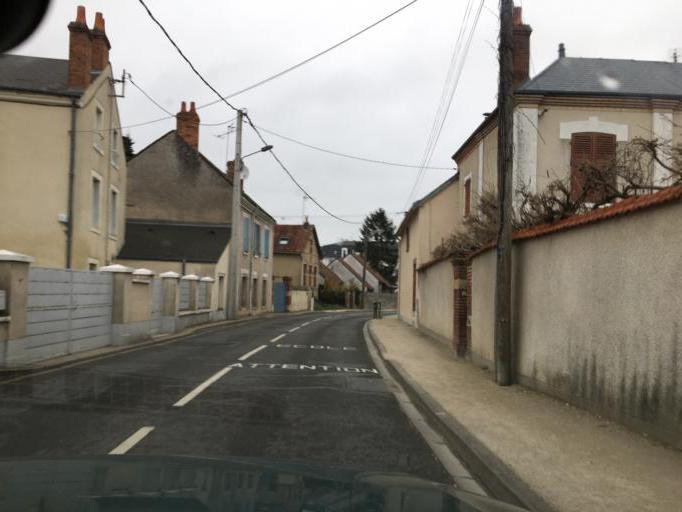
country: FR
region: Centre
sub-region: Departement du Loiret
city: Saint-Jean-le-Blanc
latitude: 47.8911
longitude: 1.9151
